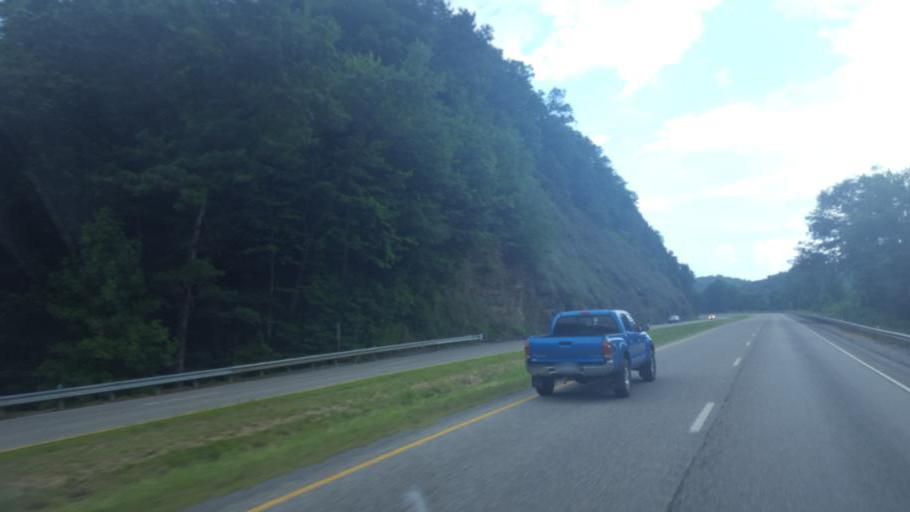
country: US
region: Virginia
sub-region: Wise County
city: Wise
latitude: 37.0327
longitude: -82.5978
